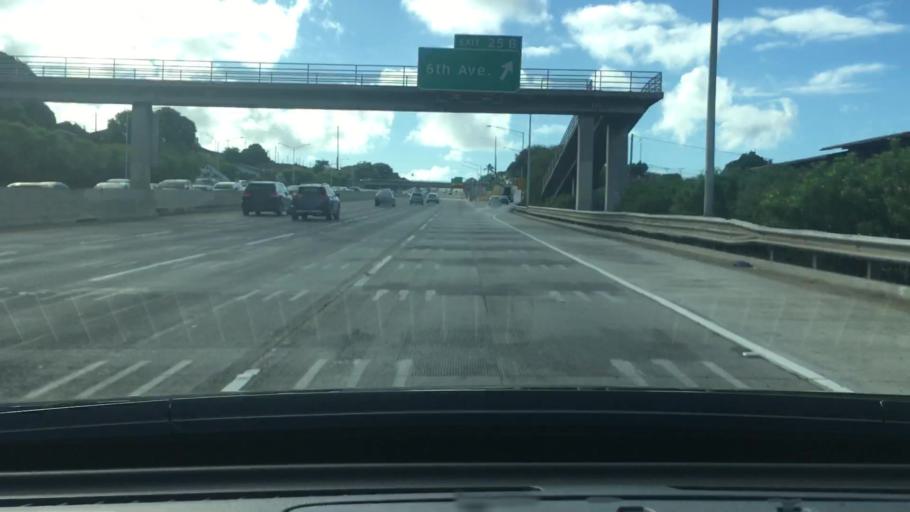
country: US
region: Hawaii
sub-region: Honolulu County
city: Honolulu
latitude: 21.2852
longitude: -157.8102
